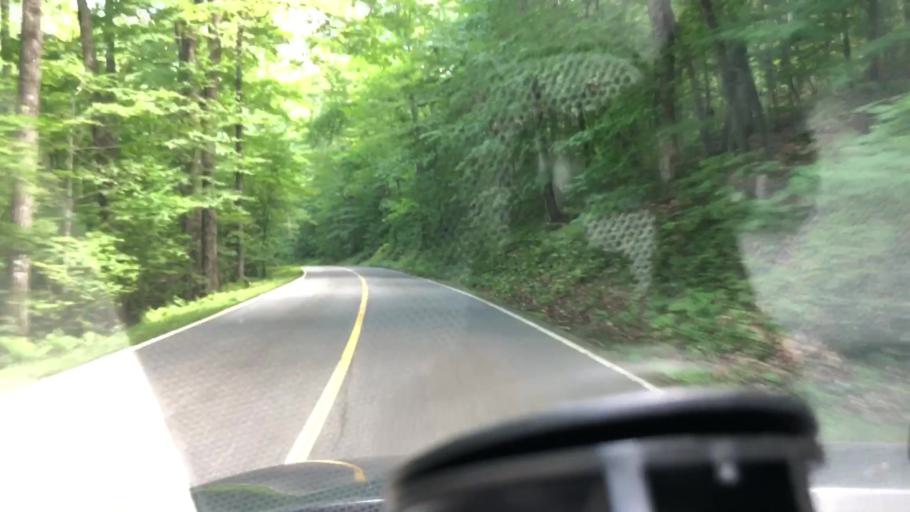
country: US
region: Massachusetts
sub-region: Berkshire County
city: North Adams
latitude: 42.6746
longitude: -73.1575
